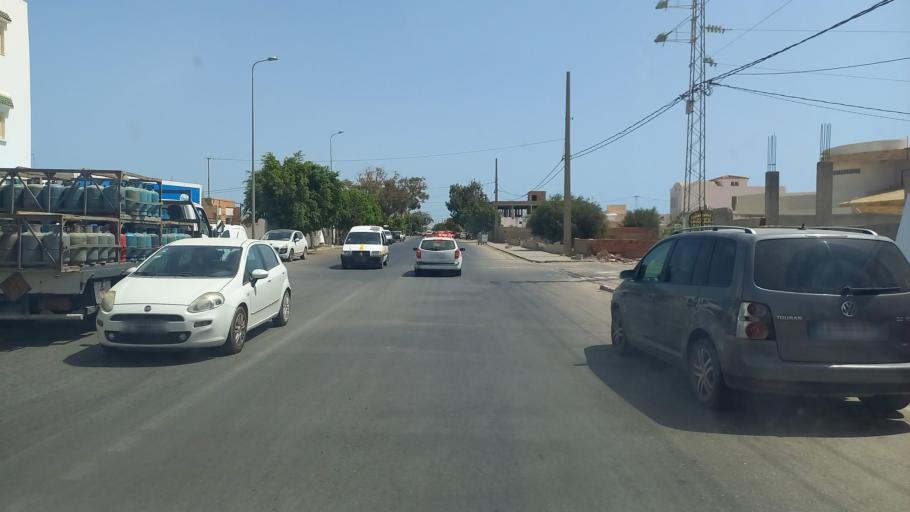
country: TN
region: Madanin
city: Zarzis
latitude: 33.4943
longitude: 11.0814
